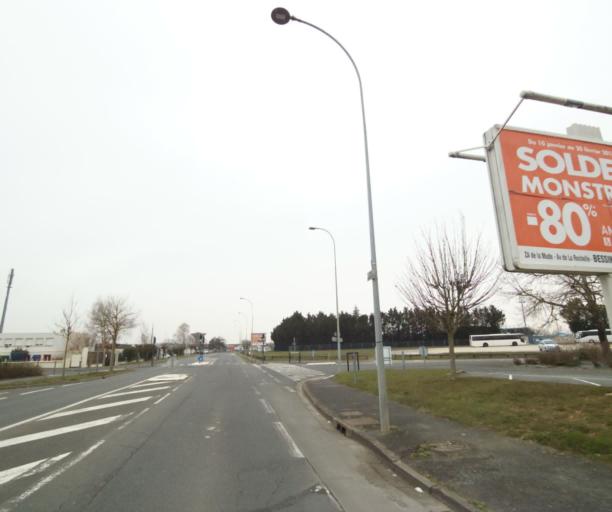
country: FR
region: Poitou-Charentes
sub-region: Departement des Deux-Sevres
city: Bessines
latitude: 46.3149
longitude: -0.4884
